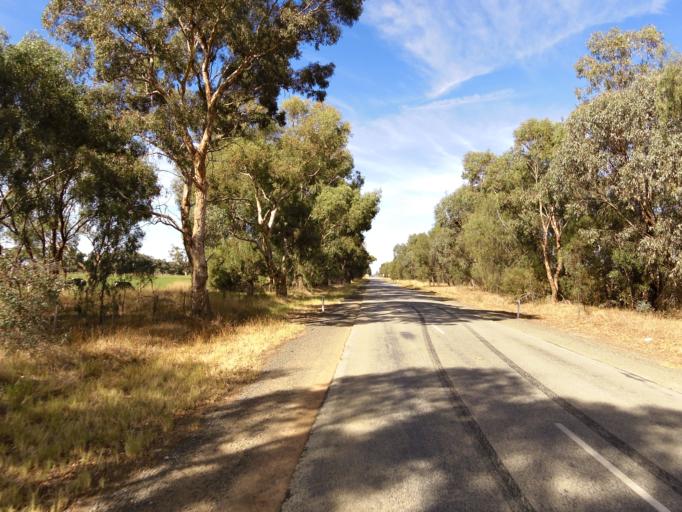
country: AU
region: Victoria
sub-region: Campaspe
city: Echuca
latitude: -36.2579
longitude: 144.5358
